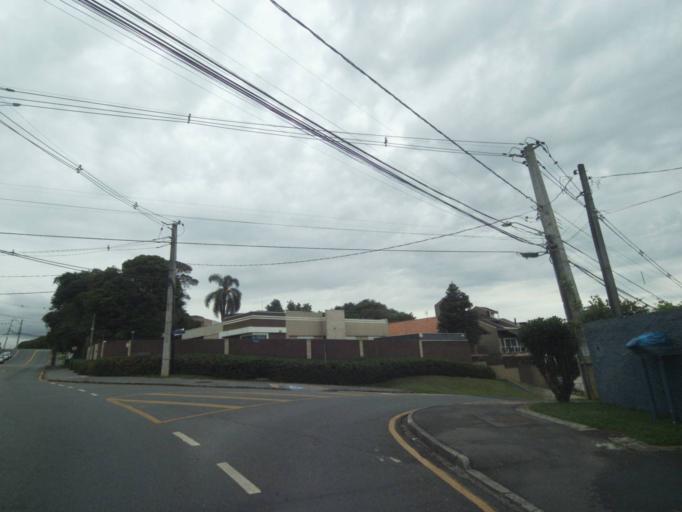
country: BR
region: Parana
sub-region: Curitiba
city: Curitiba
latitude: -25.4041
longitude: -49.2919
